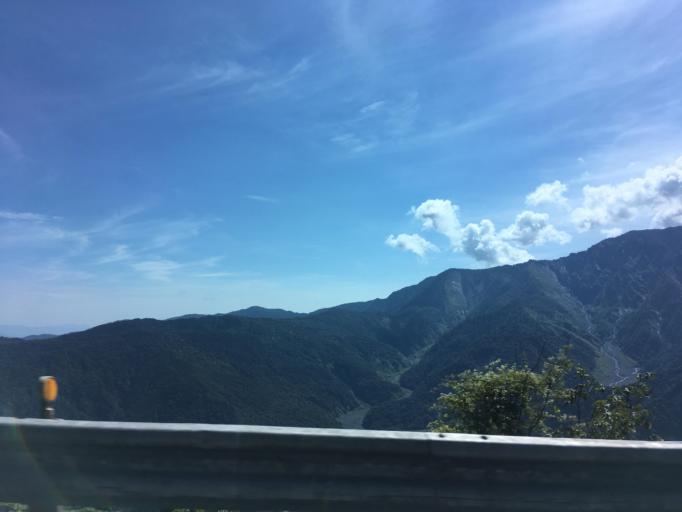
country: TW
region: Taiwan
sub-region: Yilan
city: Yilan
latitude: 24.5281
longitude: 121.5193
